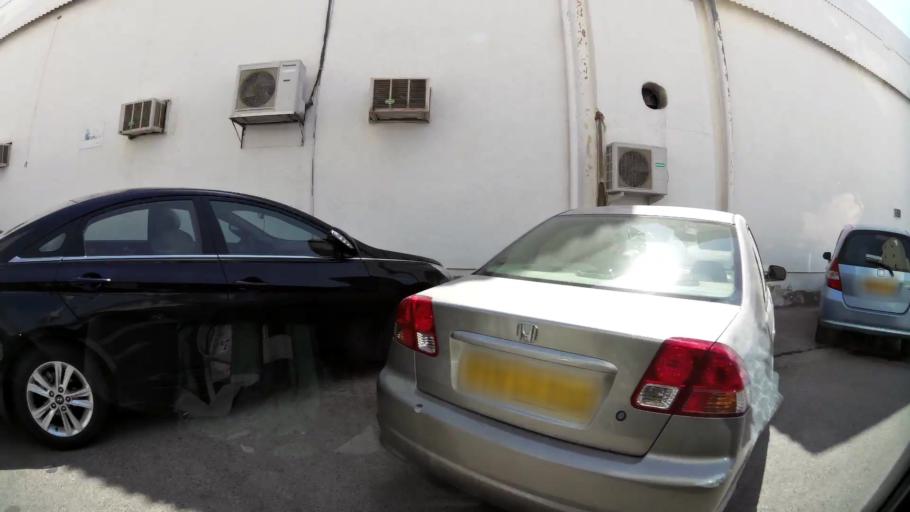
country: OM
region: Muhafazat Masqat
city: Muscat
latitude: 23.5988
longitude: 58.5393
